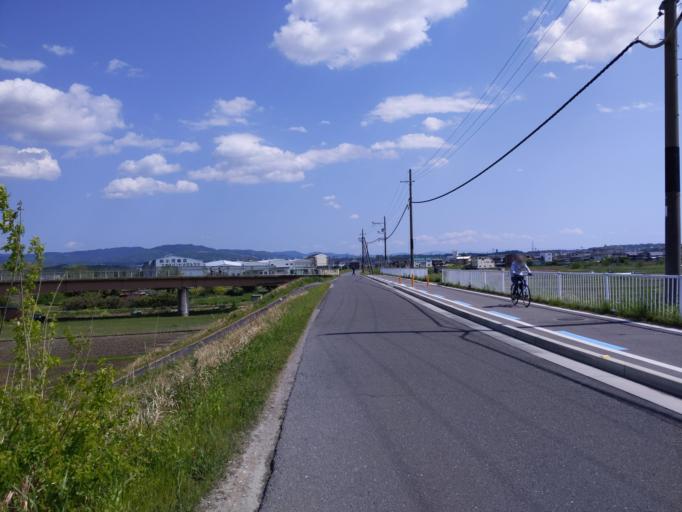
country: JP
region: Nara
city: Nara-shi
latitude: 34.7434
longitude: 135.8030
